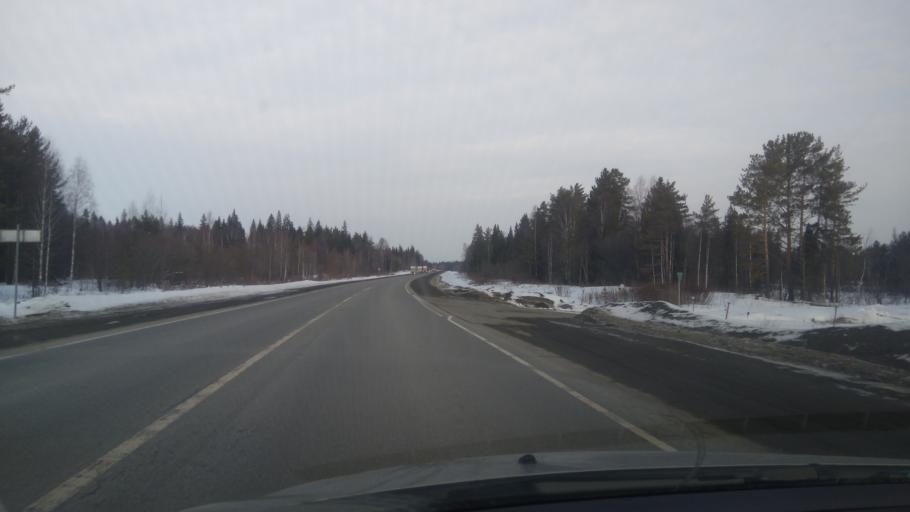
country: RU
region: Sverdlovsk
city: Atig
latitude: 56.8040
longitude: 59.3757
